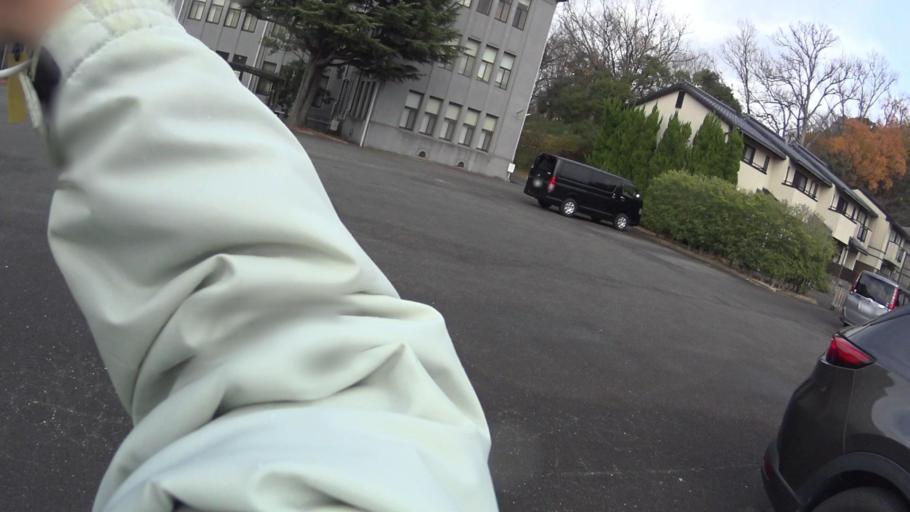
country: JP
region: Kyoto
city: Kyoto
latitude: 34.9869
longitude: 135.7767
